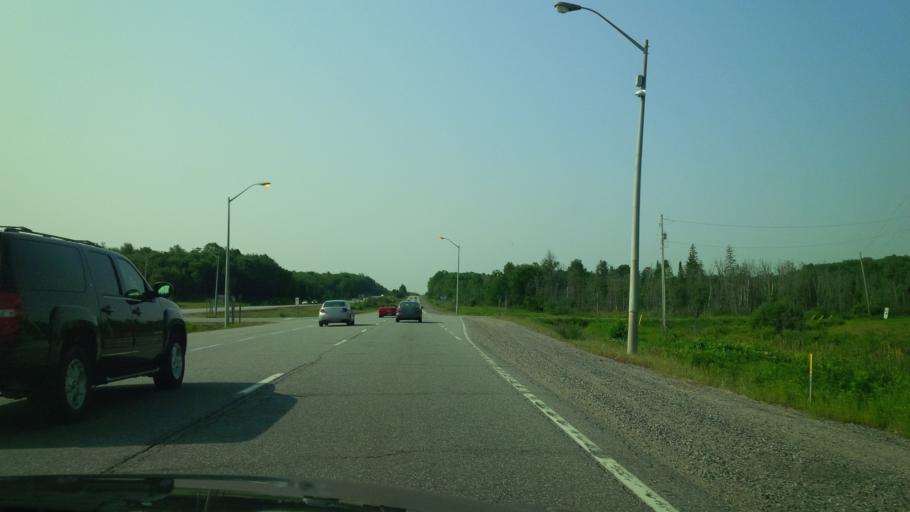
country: CA
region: Ontario
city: Bracebridge
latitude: 45.1968
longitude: -79.3140
